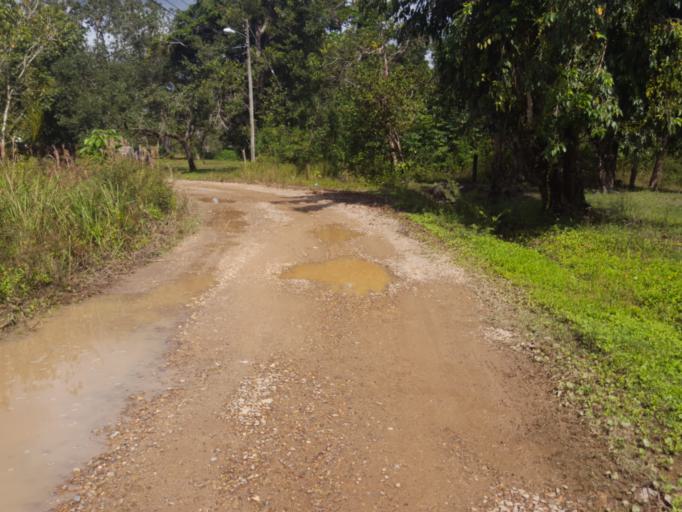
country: BZ
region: Belize
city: Belize City
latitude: 17.5713
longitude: -88.4086
